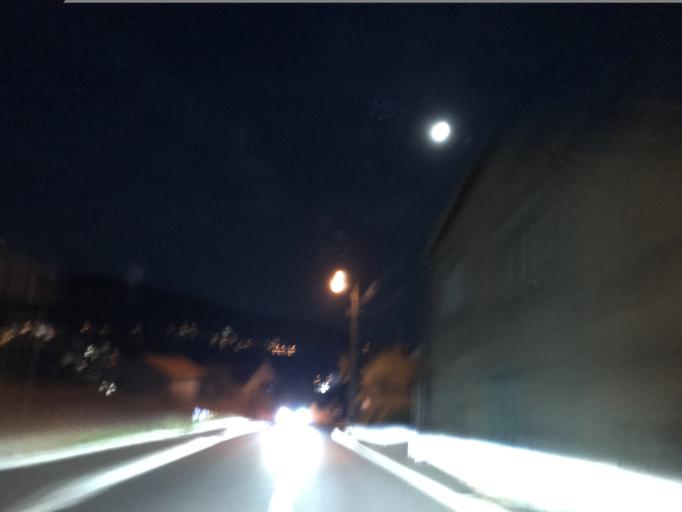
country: FR
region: Auvergne
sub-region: Departement du Puy-de-Dome
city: Thiers
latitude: 45.8595
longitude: 3.5328
